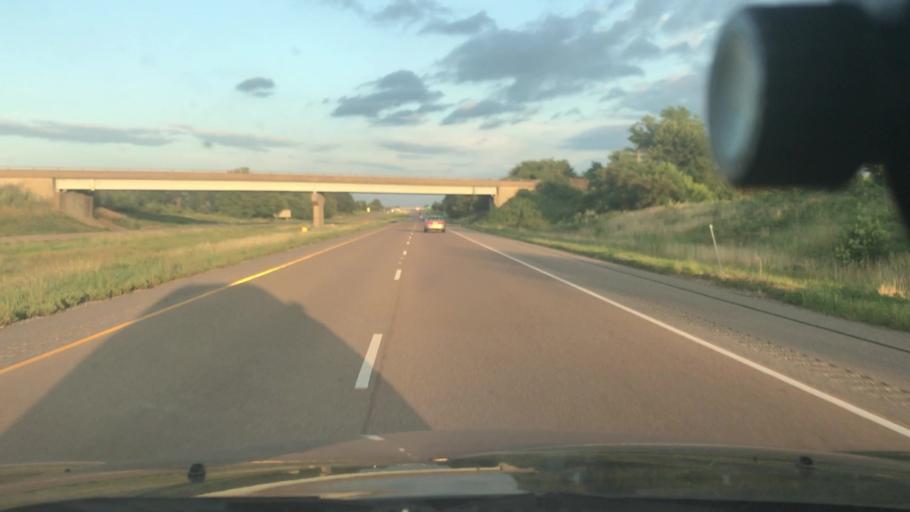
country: US
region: Illinois
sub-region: Washington County
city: Okawville
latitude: 38.4489
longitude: -89.5477
